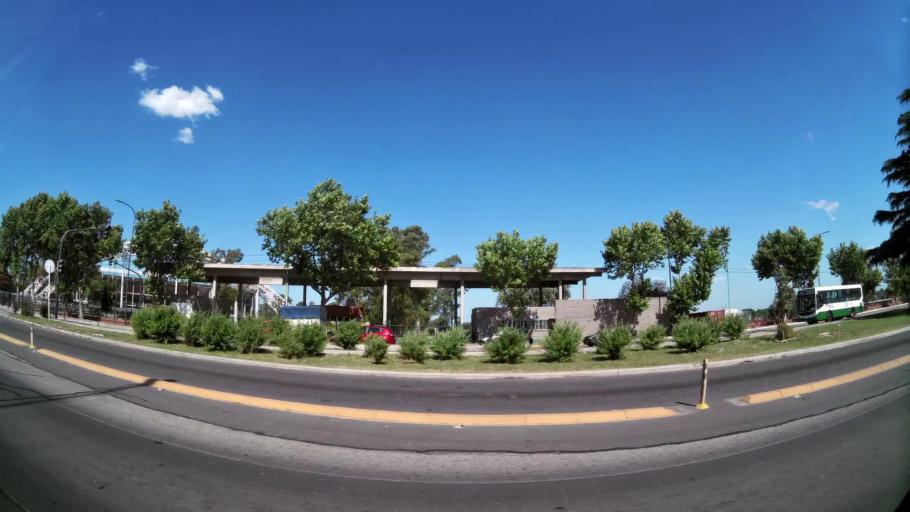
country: AR
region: Buenos Aires F.D.
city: Villa Lugano
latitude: -34.6779
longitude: -58.4494
